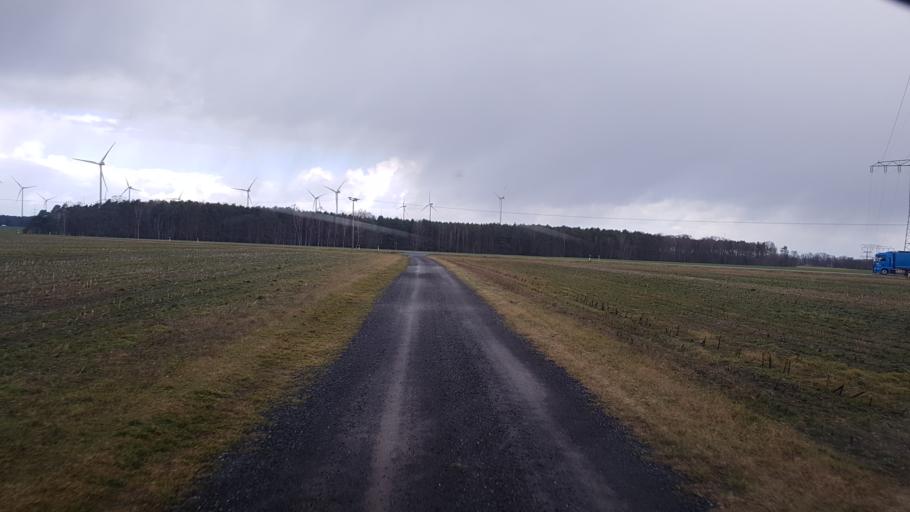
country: DE
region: Brandenburg
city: Sallgast
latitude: 51.6122
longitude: 13.8391
